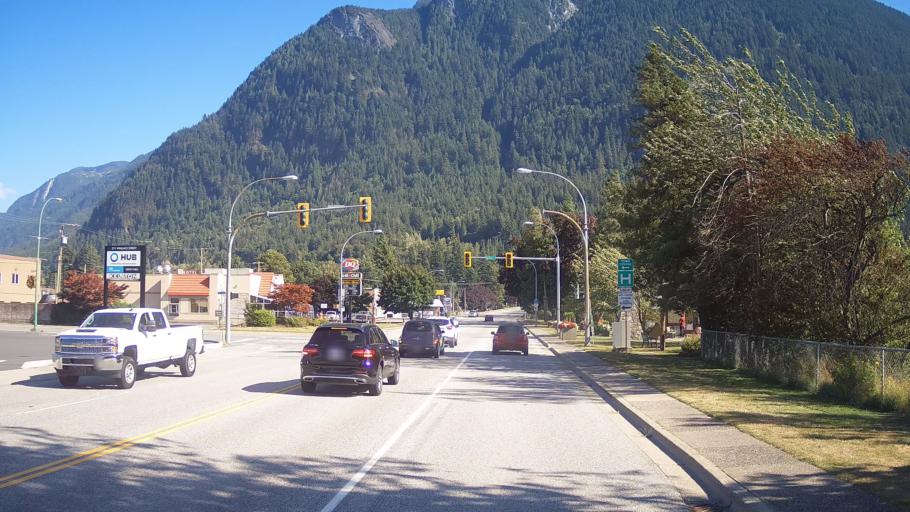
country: CA
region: British Columbia
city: Hope
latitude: 49.3789
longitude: -121.4448
